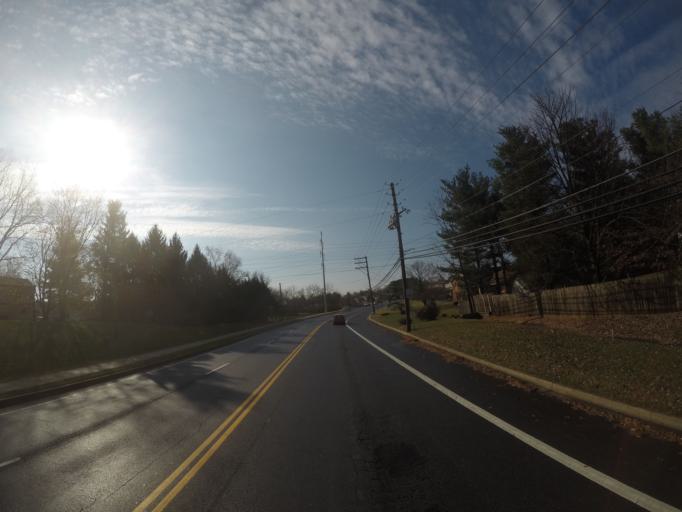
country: US
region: Maryland
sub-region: Frederick County
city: Ballenger Creek
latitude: 39.3895
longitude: -77.4406
